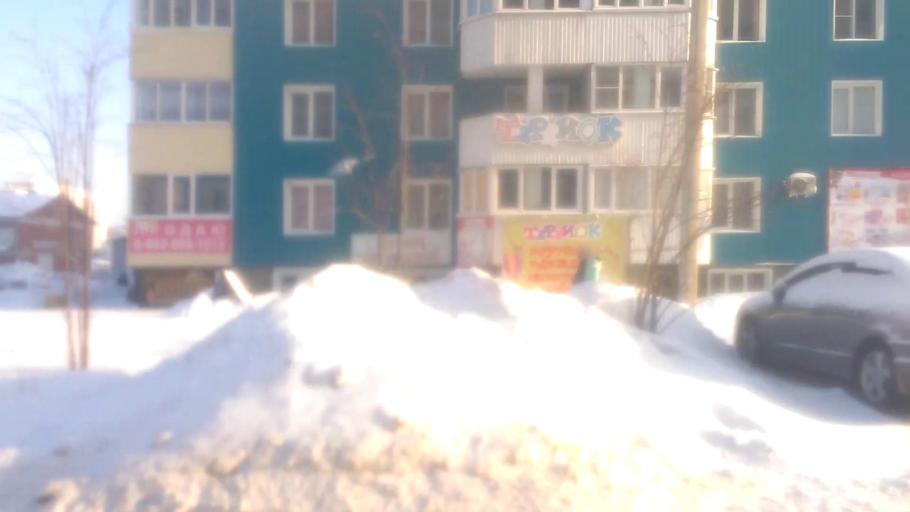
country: RU
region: Altai Krai
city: Novosilikatnyy
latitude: 53.3421
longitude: 83.6551
